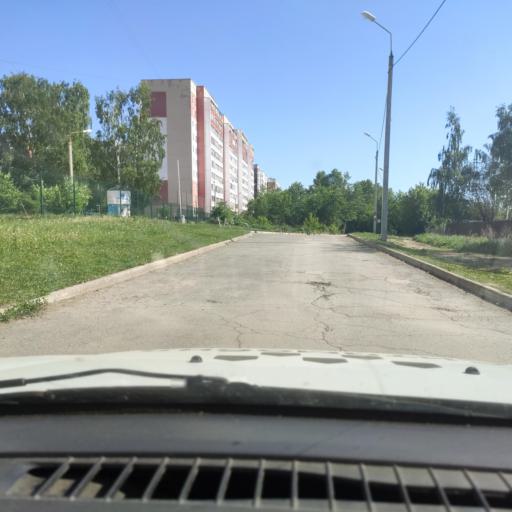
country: RU
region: Perm
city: Perm
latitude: 58.0962
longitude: 56.2995
